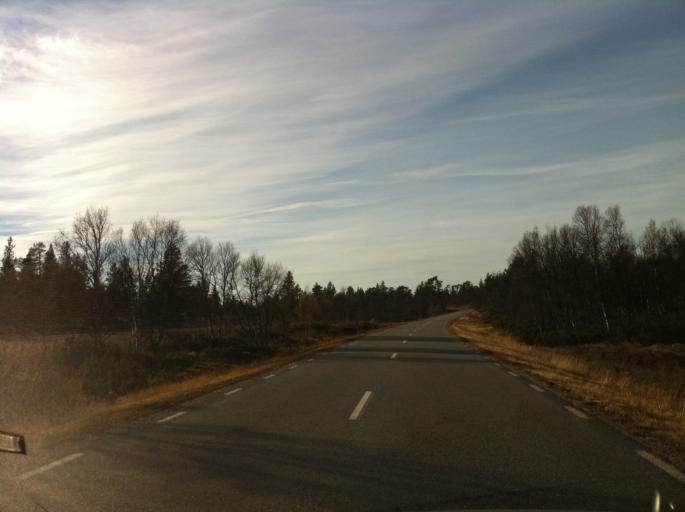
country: NO
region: Hedmark
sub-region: Engerdal
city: Engerdal
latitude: 62.0641
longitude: 12.2589
